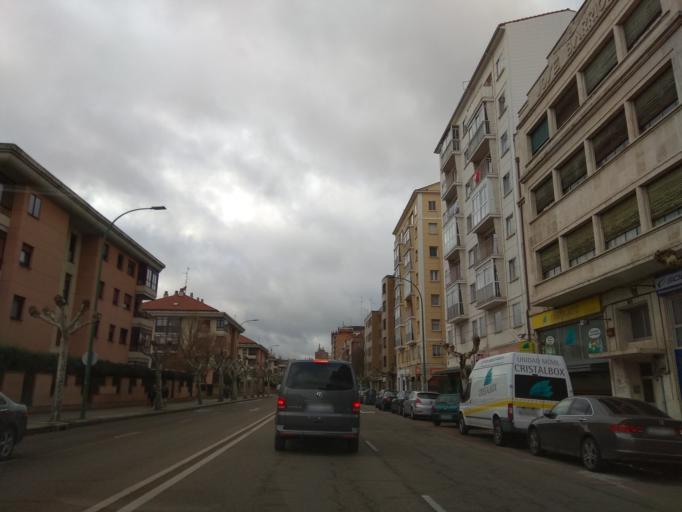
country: ES
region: Castille and Leon
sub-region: Provincia de Burgos
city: Burgos
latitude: 42.3467
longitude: -3.6812
